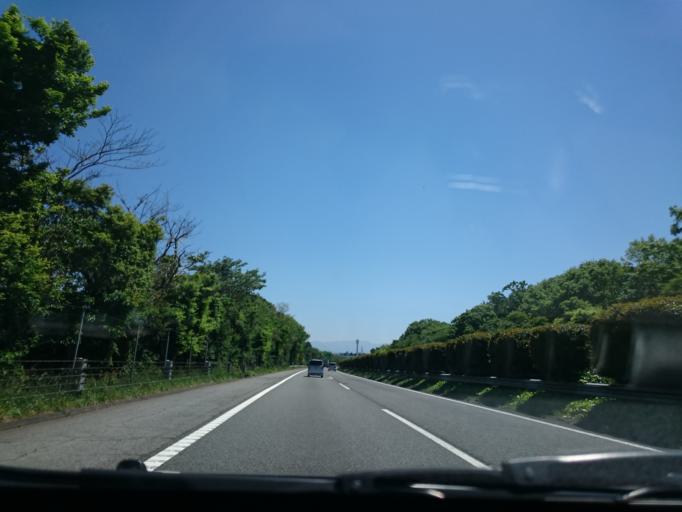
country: JP
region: Shizuoka
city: Gotemba
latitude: 35.2322
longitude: 138.9100
